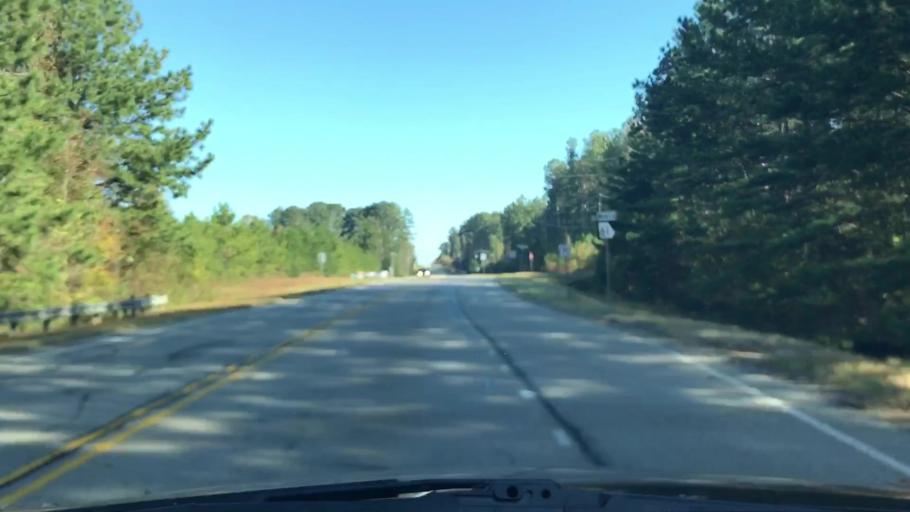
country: US
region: Georgia
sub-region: Carroll County
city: Villa Rica
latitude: 33.7795
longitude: -84.8972
